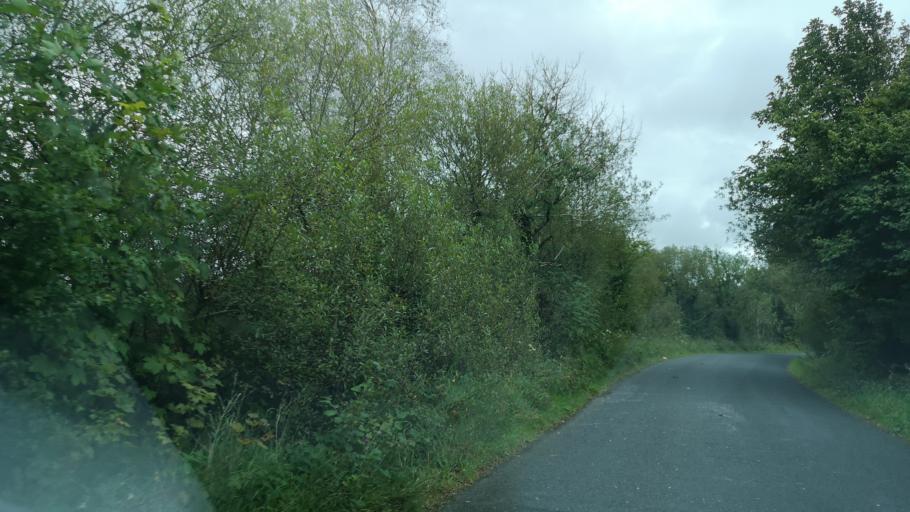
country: IE
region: Connaught
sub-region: County Galway
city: Loughrea
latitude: 53.2900
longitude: -8.5911
